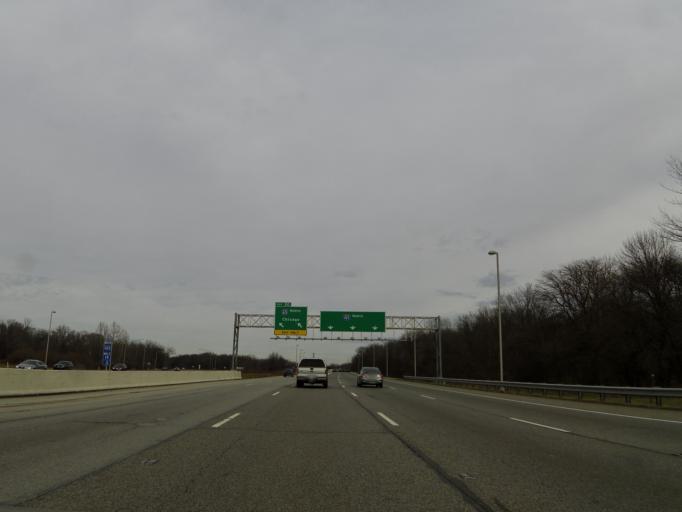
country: US
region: Indiana
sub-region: Marion County
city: Speedway
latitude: 39.8560
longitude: -86.2761
